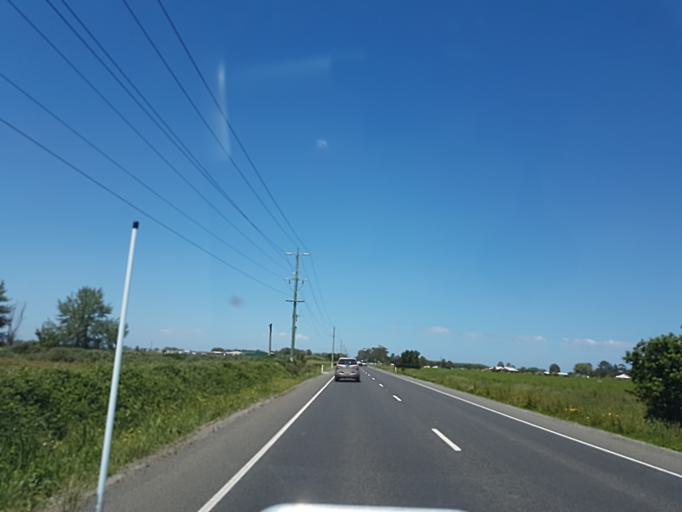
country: AU
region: Victoria
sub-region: Cardinia
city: Pakenham South
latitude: -38.1498
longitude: 145.4864
